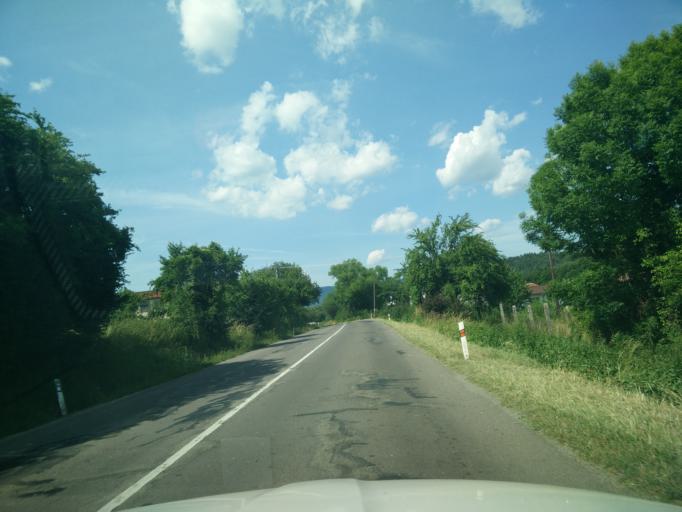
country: SK
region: Nitriansky
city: Prievidza
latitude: 48.8807
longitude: 18.6379
